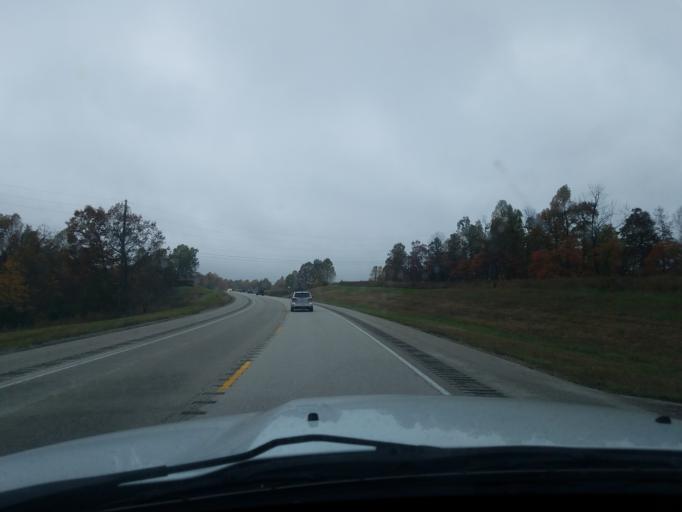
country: US
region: Kentucky
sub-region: Larue County
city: Hodgenville
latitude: 37.4646
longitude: -85.5709
